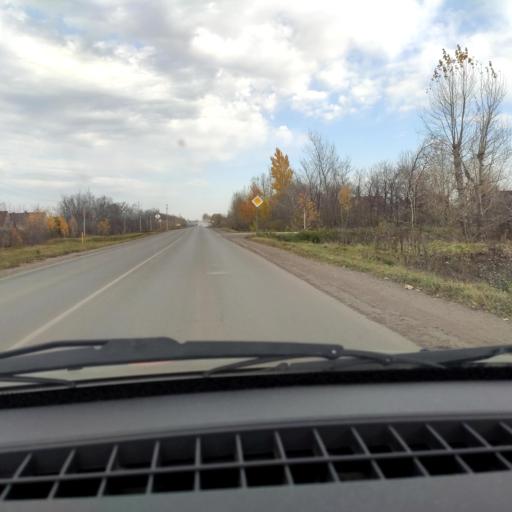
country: RU
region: Bashkortostan
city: Ufa
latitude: 54.6230
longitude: 55.9100
